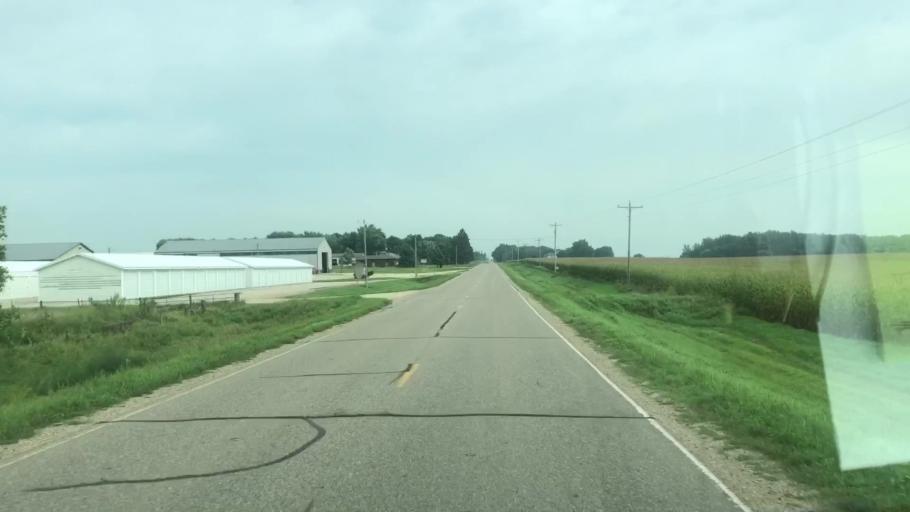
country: US
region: Iowa
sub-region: O'Brien County
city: Sheldon
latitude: 43.1926
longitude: -95.8622
